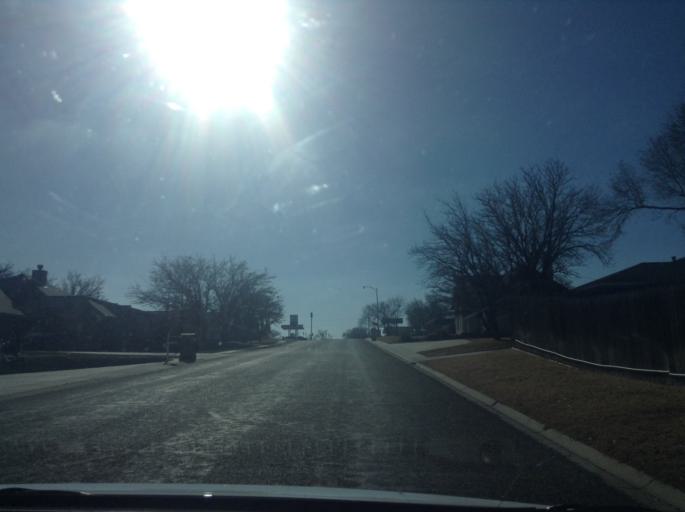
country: US
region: Texas
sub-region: Randall County
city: Canyon
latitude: 34.9881
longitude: -101.9288
